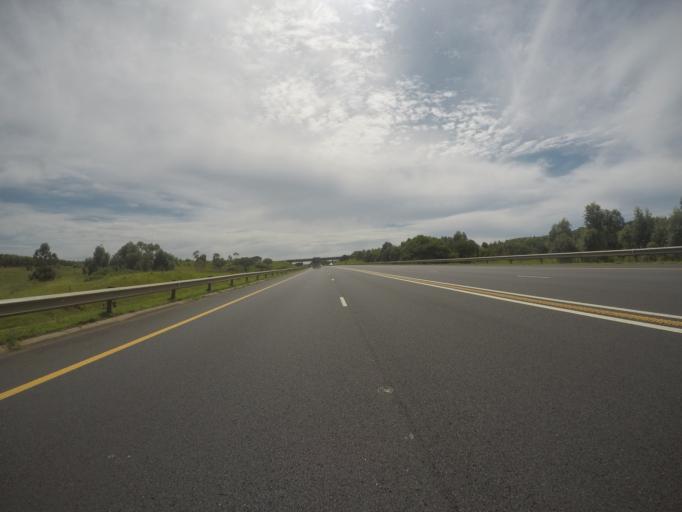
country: ZA
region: KwaZulu-Natal
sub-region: iLembe District Municipality
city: Mandeni
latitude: -29.1639
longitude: 31.5309
